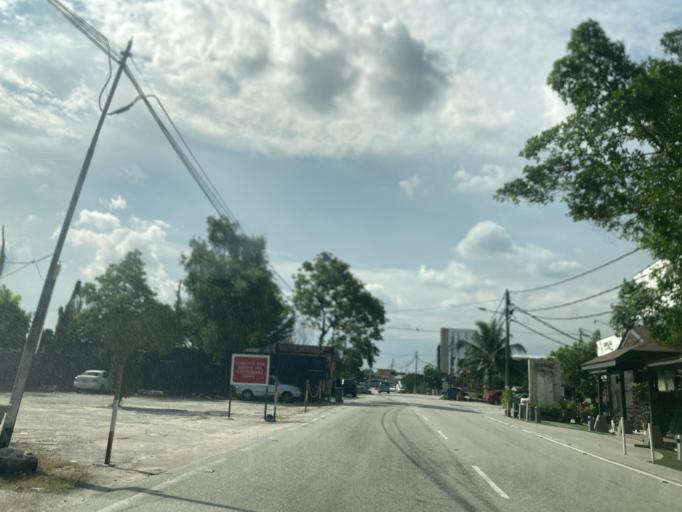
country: MY
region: Selangor
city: Kampung Baru Subang
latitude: 3.1404
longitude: 101.5468
